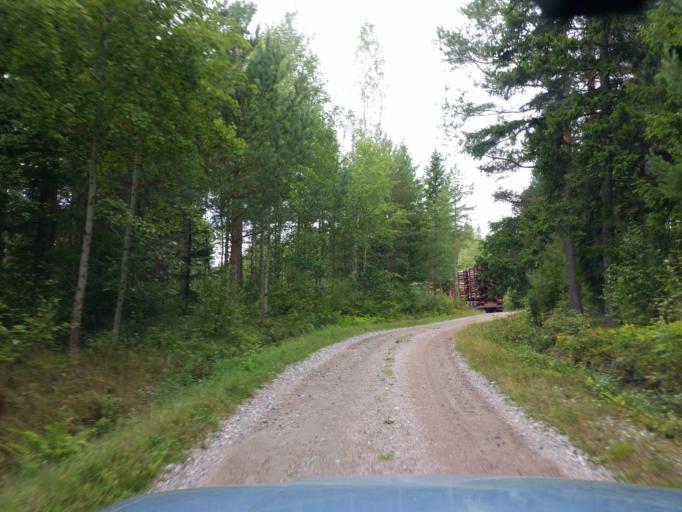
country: FI
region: Varsinais-Suomi
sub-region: Aboland-Turunmaa
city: Nagu
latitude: 60.2046
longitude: 22.0900
